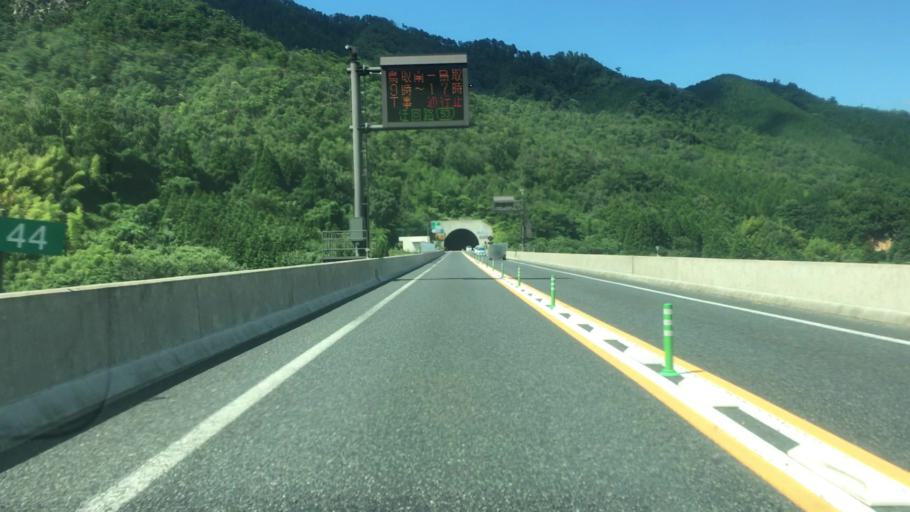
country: JP
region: Tottori
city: Tottori
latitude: 35.3373
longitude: 134.1872
